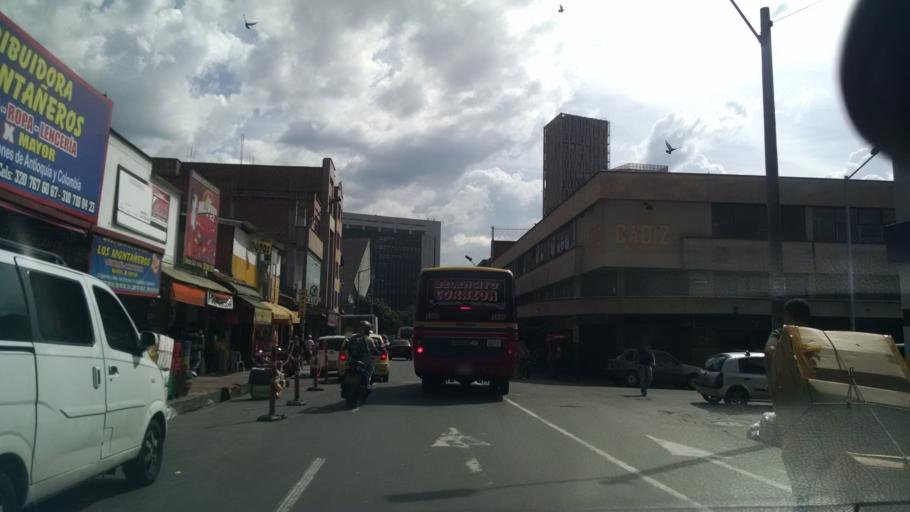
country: CO
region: Antioquia
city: Medellin
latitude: 6.2478
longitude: -75.5729
